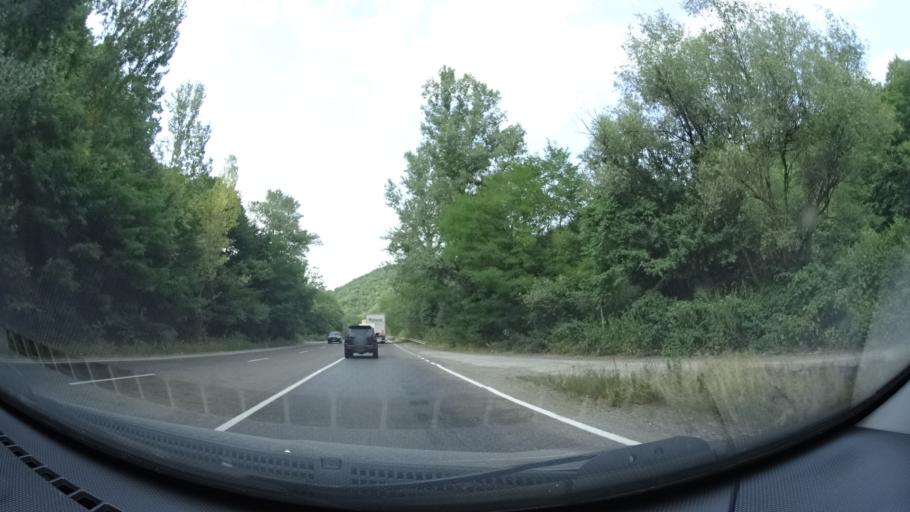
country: GE
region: Kakheti
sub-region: Gurjaani
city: Gurjaani
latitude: 41.6652
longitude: 45.8330
